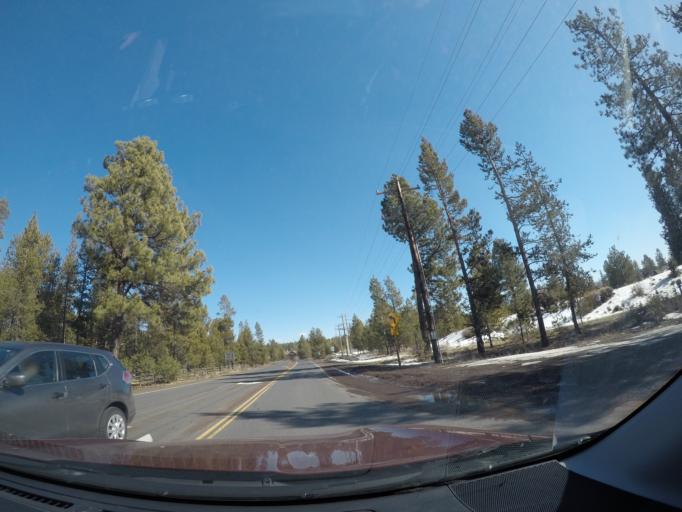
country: US
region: Oregon
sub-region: Deschutes County
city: Sunriver
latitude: 43.8634
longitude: -121.4408
